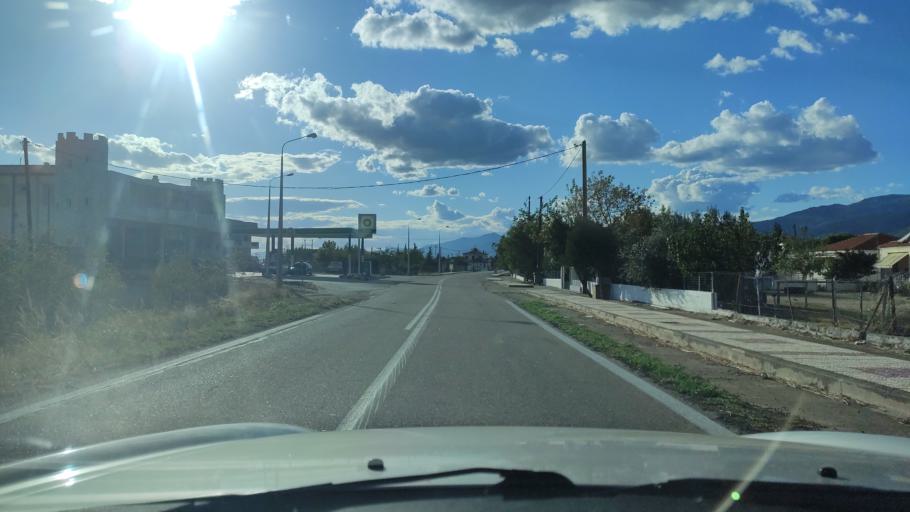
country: GR
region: East Macedonia and Thrace
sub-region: Nomos Xanthis
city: Selero
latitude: 41.1222
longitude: 25.0683
